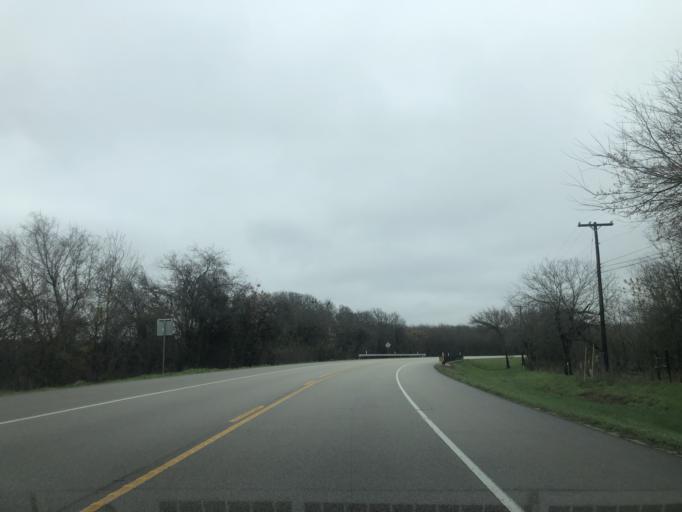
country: US
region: Texas
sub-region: Williamson County
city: Georgetown
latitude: 30.6467
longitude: -97.5822
